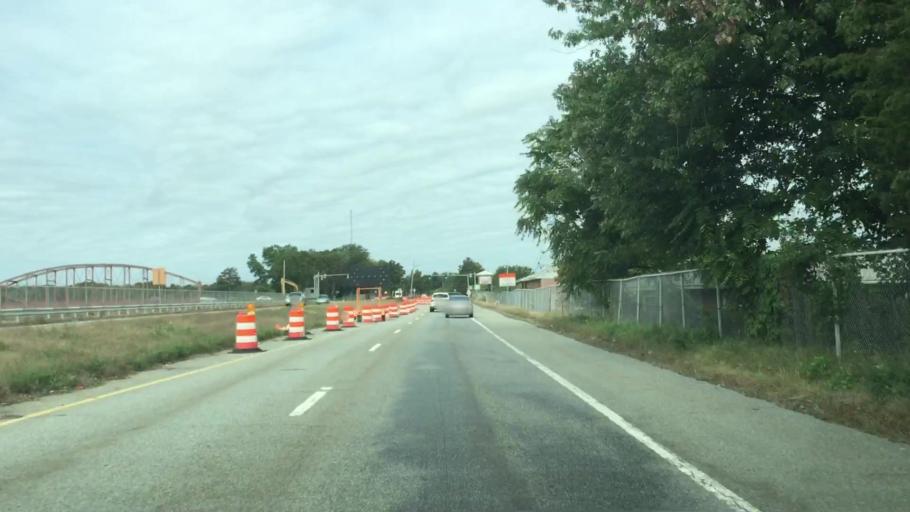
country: US
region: Massachusetts
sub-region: Middlesex County
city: Dracut
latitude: 42.6542
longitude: -71.3122
